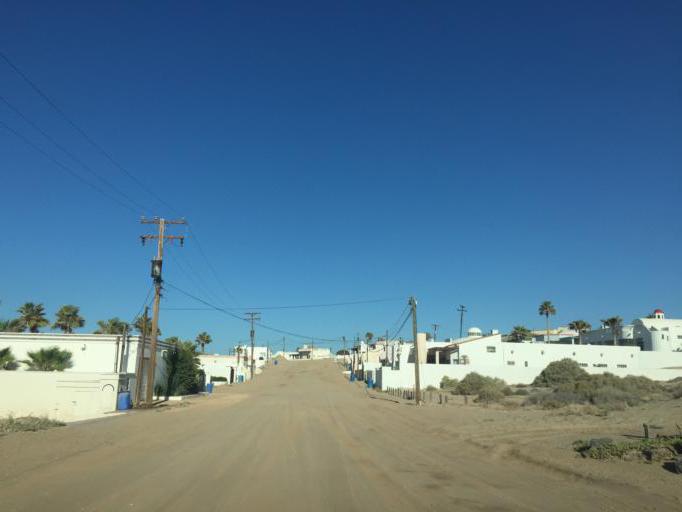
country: MX
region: Sonora
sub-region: Puerto Penasco
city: Puerto Penasco
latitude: 31.2885
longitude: -113.4840
